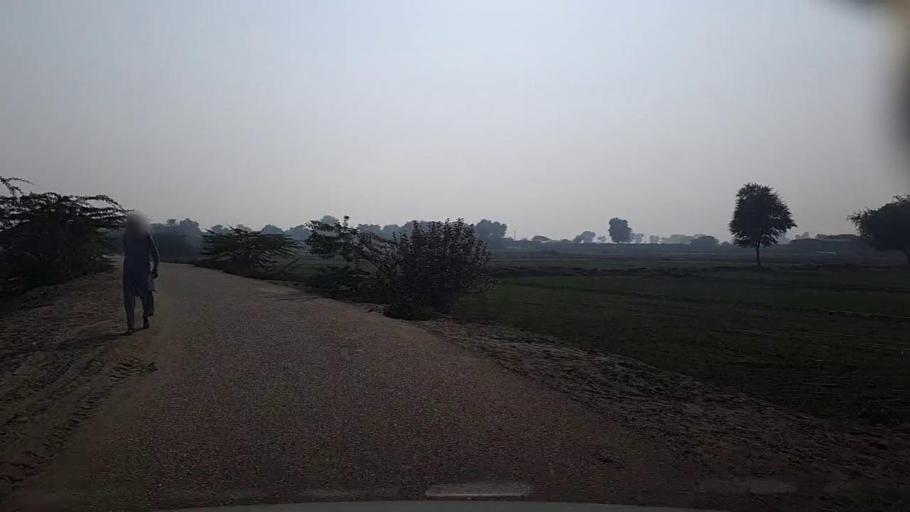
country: PK
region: Sindh
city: Kandiari
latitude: 27.0522
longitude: 68.4616
